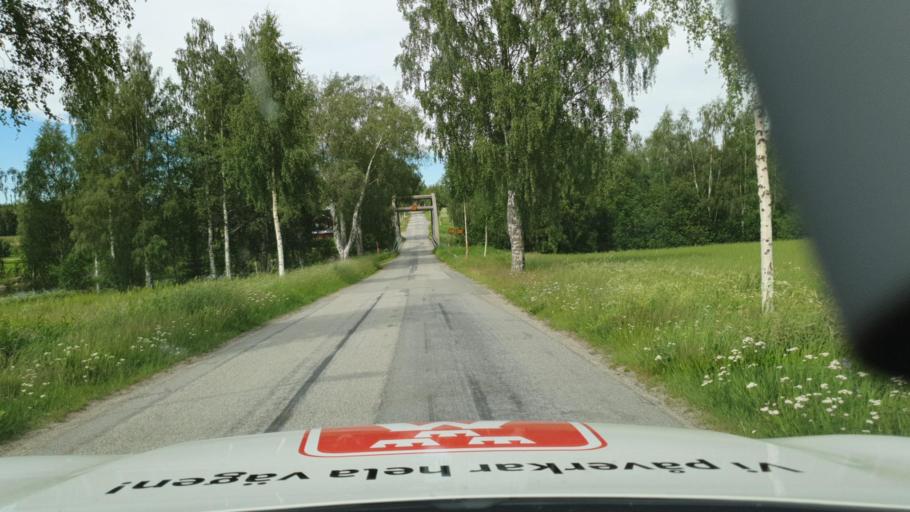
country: SE
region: Vaesterbotten
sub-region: Skelleftea Kommun
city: Burtraesk
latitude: 64.4517
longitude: 20.4813
